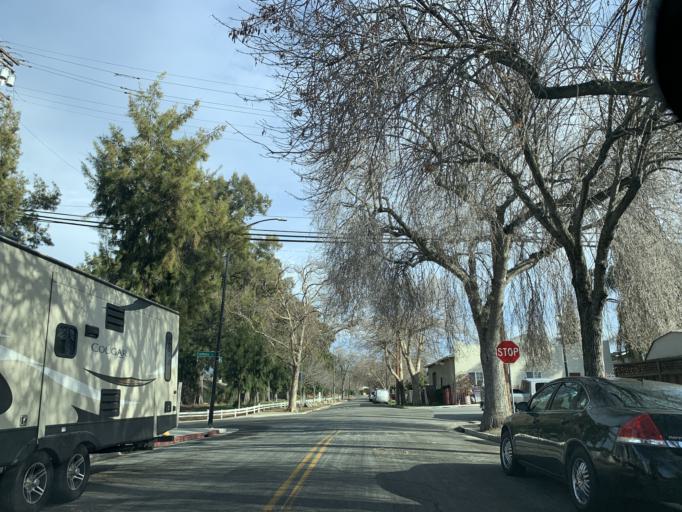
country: US
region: California
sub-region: Santa Clara County
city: San Jose
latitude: 37.3178
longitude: -121.8936
